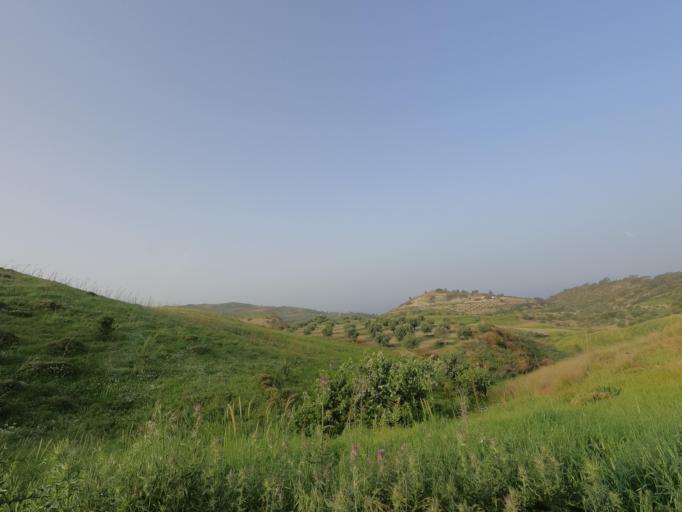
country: CY
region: Pafos
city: Polis
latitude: 34.9883
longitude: 32.3350
